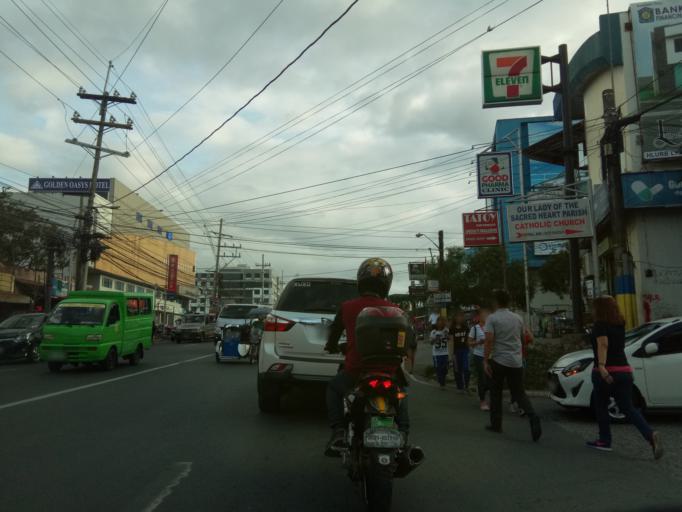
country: PH
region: Calabarzon
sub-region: Province of Cavite
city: Imus
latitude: 14.3852
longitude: 120.9779
